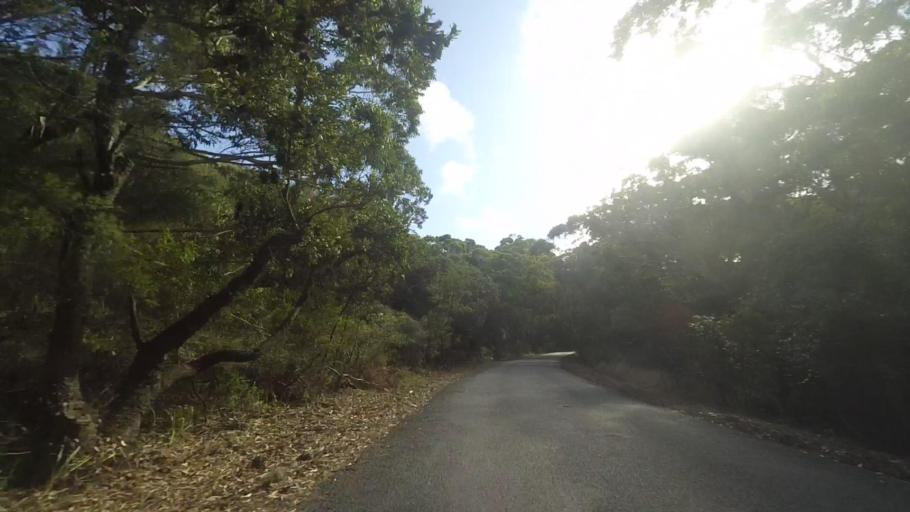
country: AU
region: New South Wales
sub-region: Great Lakes
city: Forster
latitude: -32.4320
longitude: 152.5200
